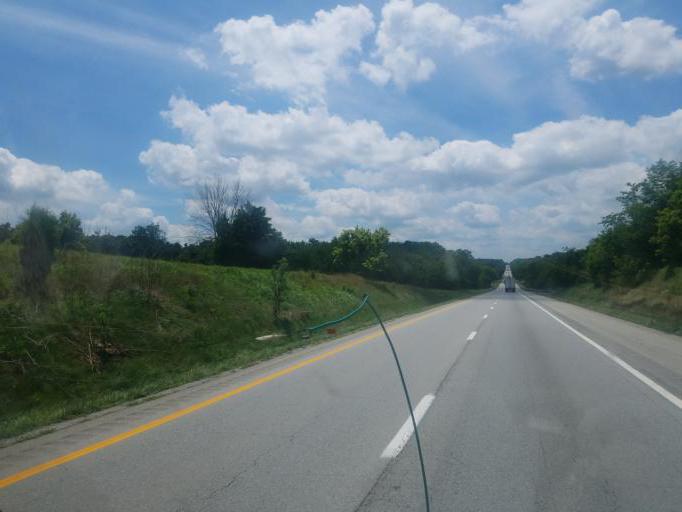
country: US
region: Kentucky
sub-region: Oldham County
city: La Grange
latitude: 38.4278
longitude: -85.3245
